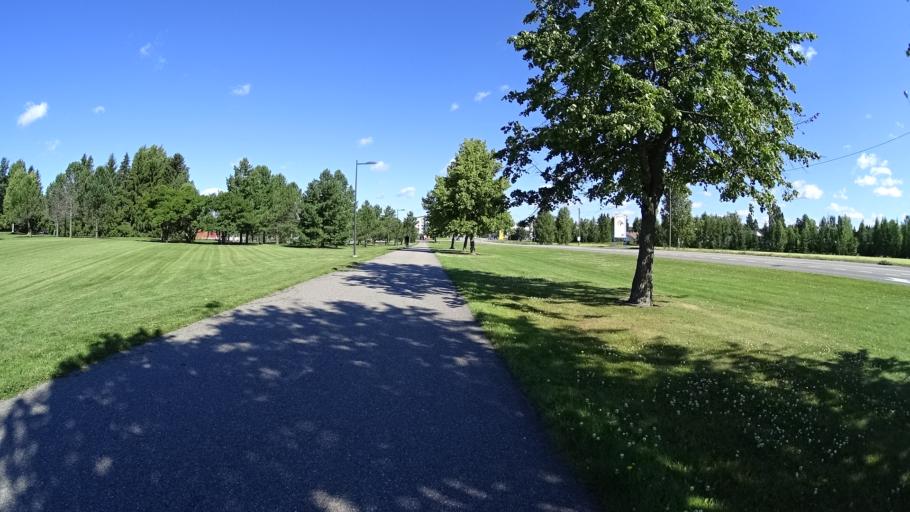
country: FI
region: Uusimaa
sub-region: Helsinki
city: Jaervenpaeae
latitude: 60.4632
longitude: 25.0861
